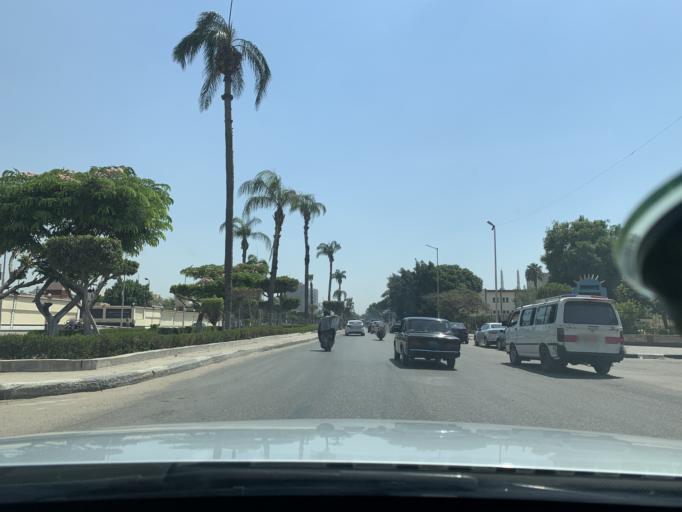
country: EG
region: Muhafazat al Qahirah
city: Cairo
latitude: 30.0800
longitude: 31.2913
